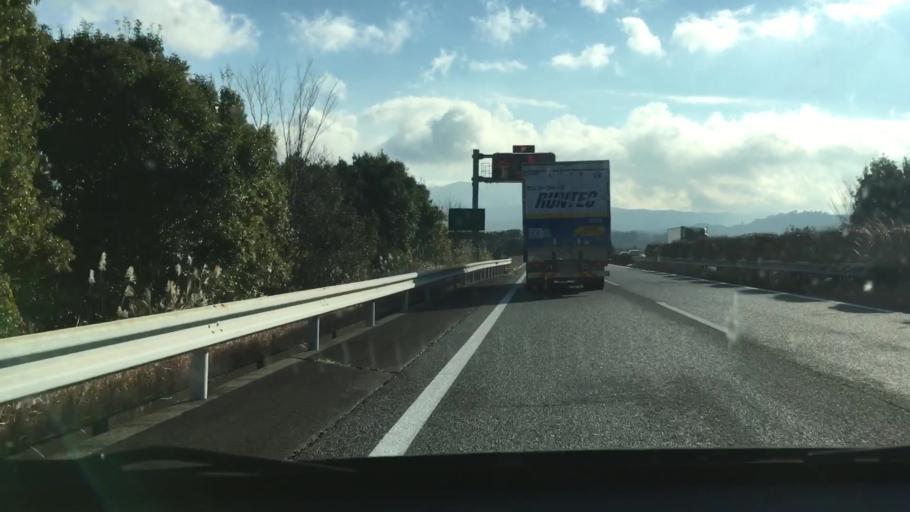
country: JP
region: Kumamoto
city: Hitoyoshi
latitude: 32.0560
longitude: 130.8025
